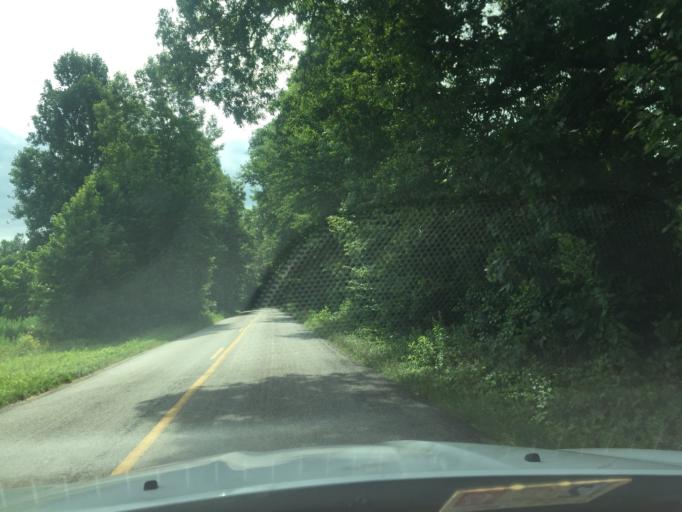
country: US
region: Virginia
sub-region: Charles City County
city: Charles City
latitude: 37.4115
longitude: -77.0372
